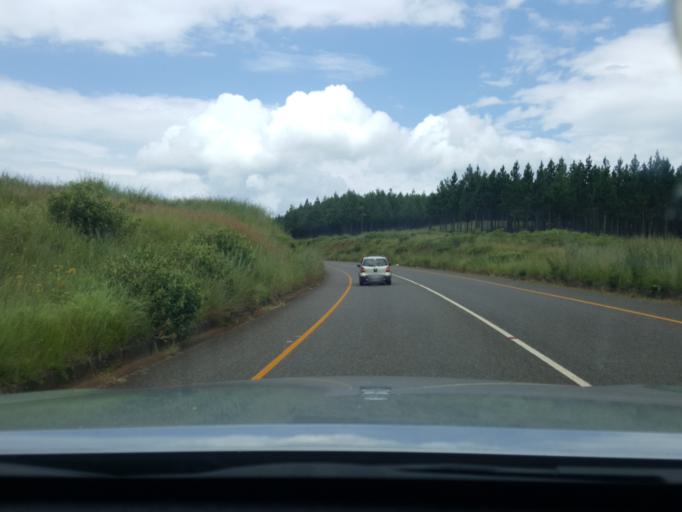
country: ZA
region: Mpumalanga
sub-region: Ehlanzeni District
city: Graksop
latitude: -25.1304
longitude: 30.8116
